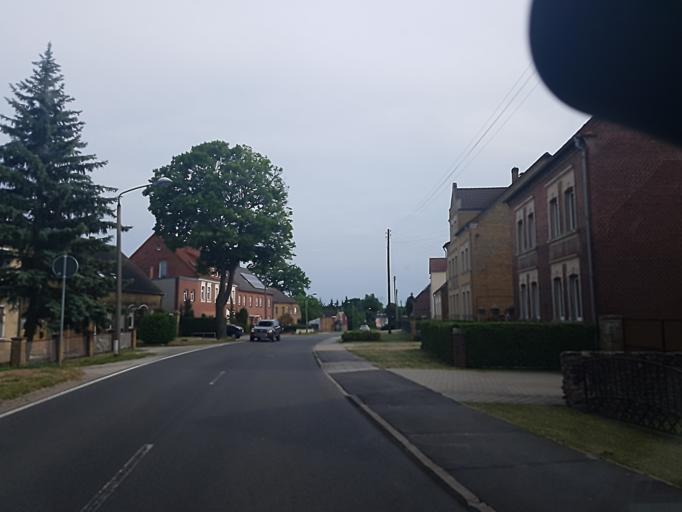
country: DE
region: Saxony-Anhalt
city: Nudersdorf
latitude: 51.9066
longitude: 12.6108
